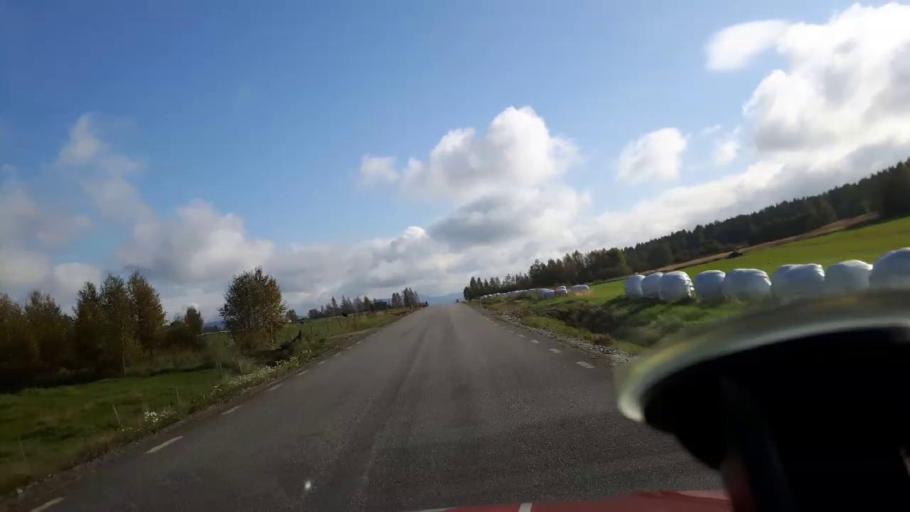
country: SE
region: Gaevleborg
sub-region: Ljusdals Kommun
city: Ljusdal
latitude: 61.7639
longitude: 16.0589
